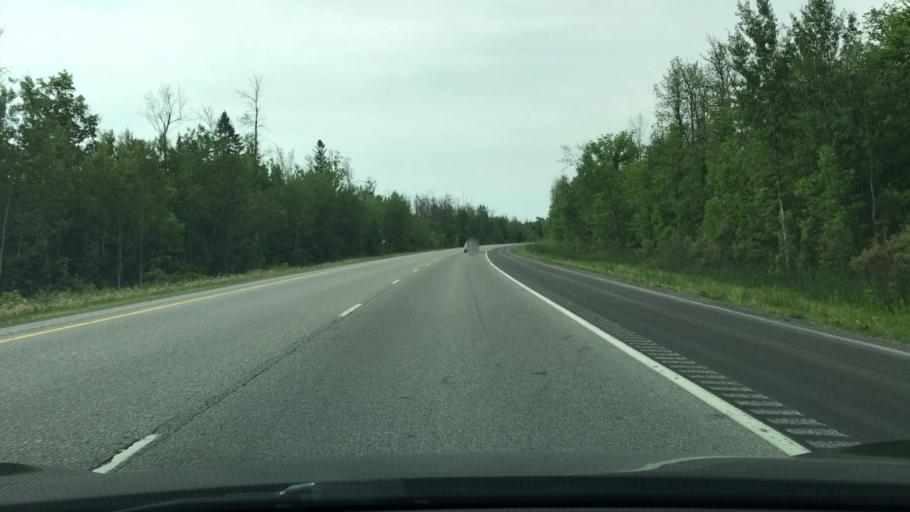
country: CA
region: Ontario
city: Prescott
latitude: 44.9352
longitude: -75.5762
